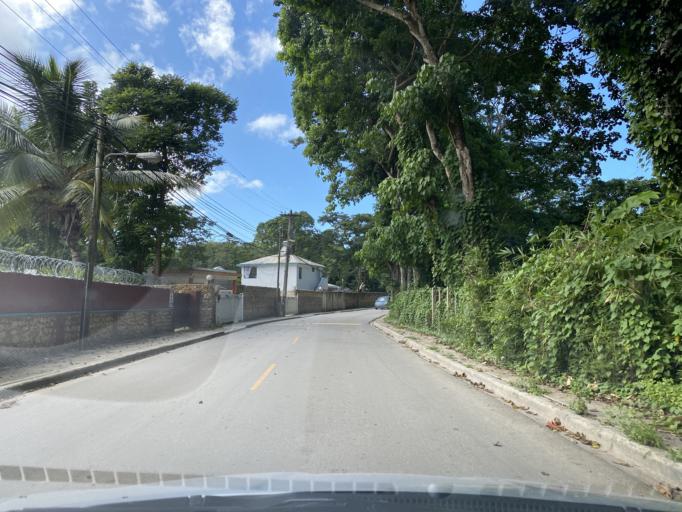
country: DO
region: Samana
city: Las Terrenas
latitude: 19.3071
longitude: -69.5624
